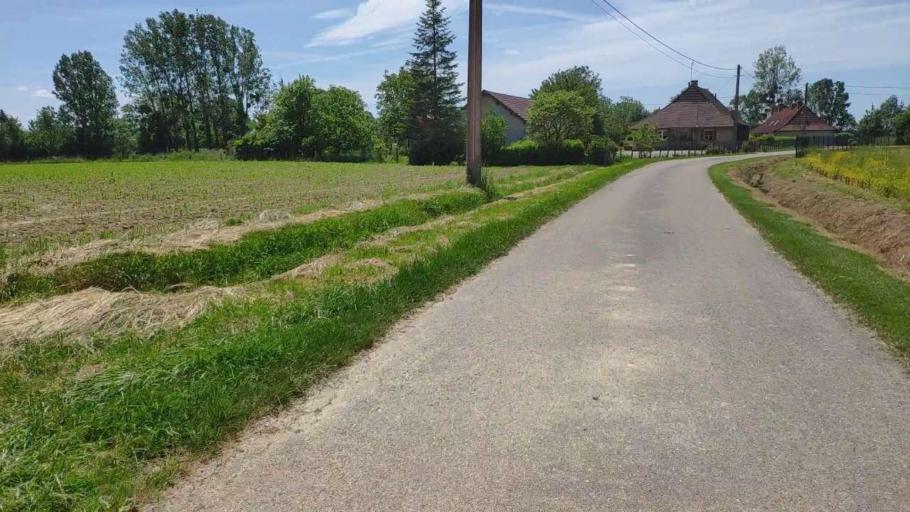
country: FR
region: Franche-Comte
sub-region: Departement du Jura
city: Bletterans
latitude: 46.8031
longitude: 5.3882
